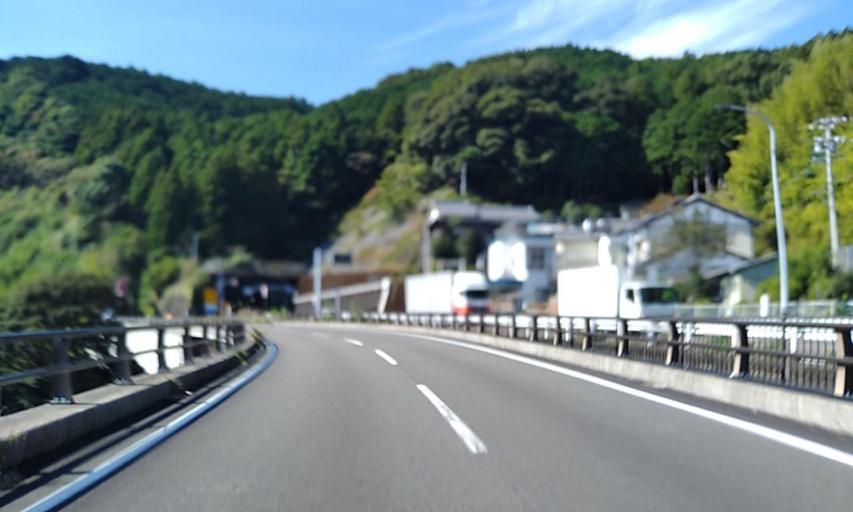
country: JP
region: Mie
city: Owase
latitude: 33.8957
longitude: 136.1156
